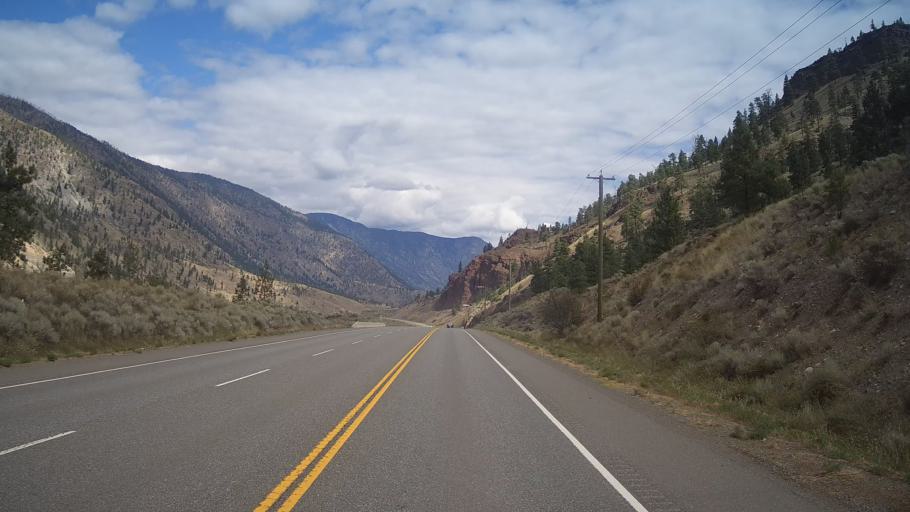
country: CA
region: British Columbia
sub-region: Thompson-Nicola Regional District
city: Ashcroft
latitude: 50.2998
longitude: -121.3923
